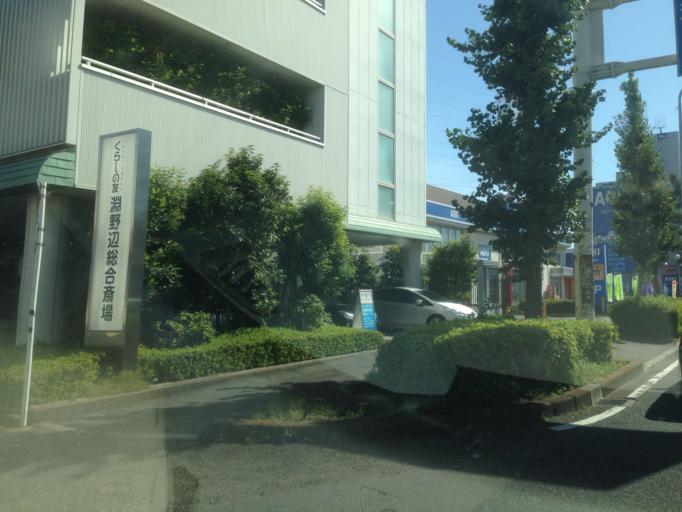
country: JP
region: Tokyo
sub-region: Machida-shi
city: Machida
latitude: 35.5662
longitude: 139.3886
